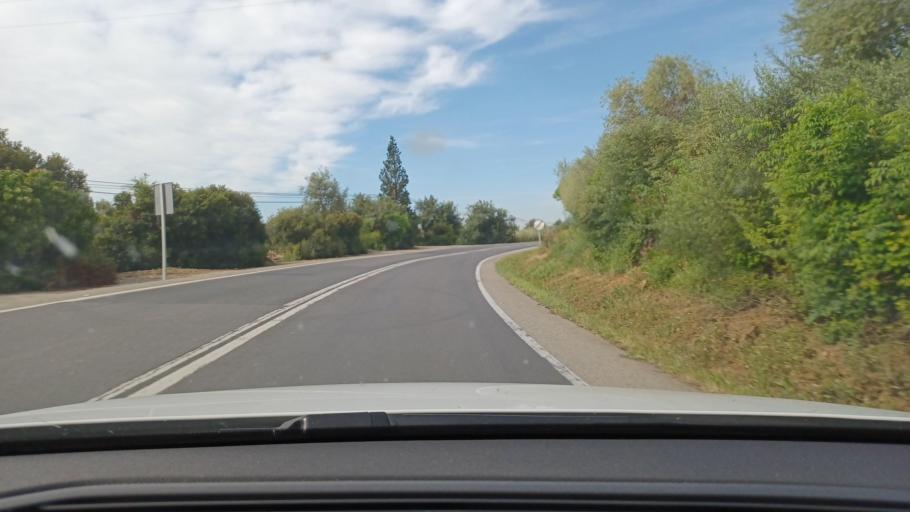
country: ES
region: Catalonia
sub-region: Provincia de Tarragona
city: Santa Barbara
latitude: 40.6918
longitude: 0.4746
